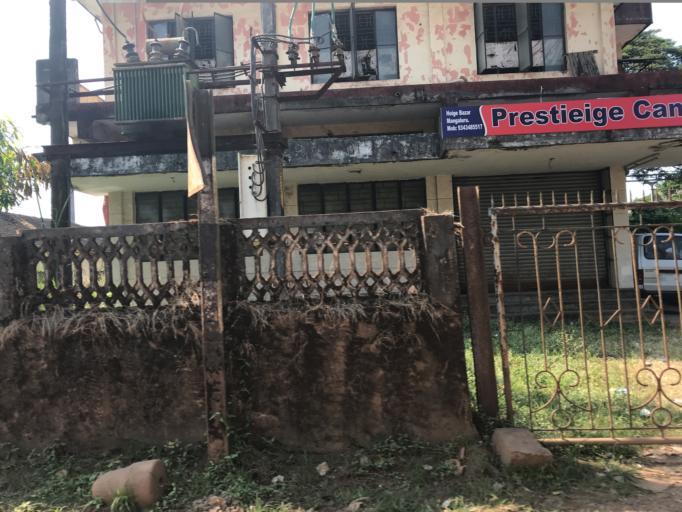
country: IN
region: Karnataka
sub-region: Dakshina Kannada
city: Ullal
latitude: 12.8533
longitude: 74.8377
